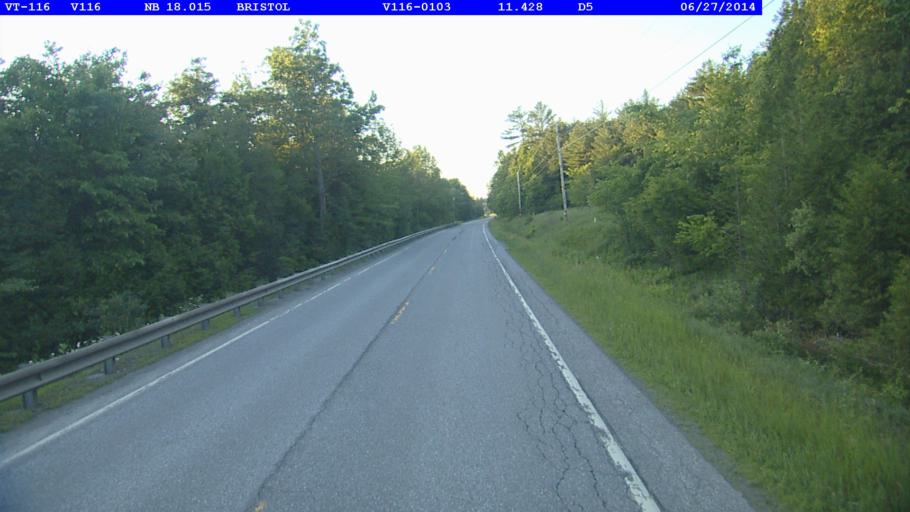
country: US
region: Vermont
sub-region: Addison County
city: Bristol
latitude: 44.1737
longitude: -73.0569
